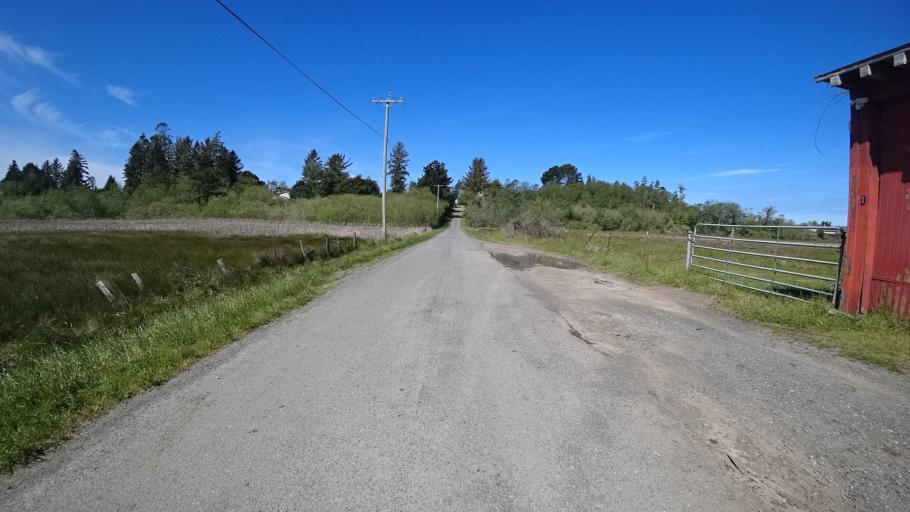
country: US
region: California
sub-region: Humboldt County
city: Myrtletown
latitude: 40.7951
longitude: -124.1223
